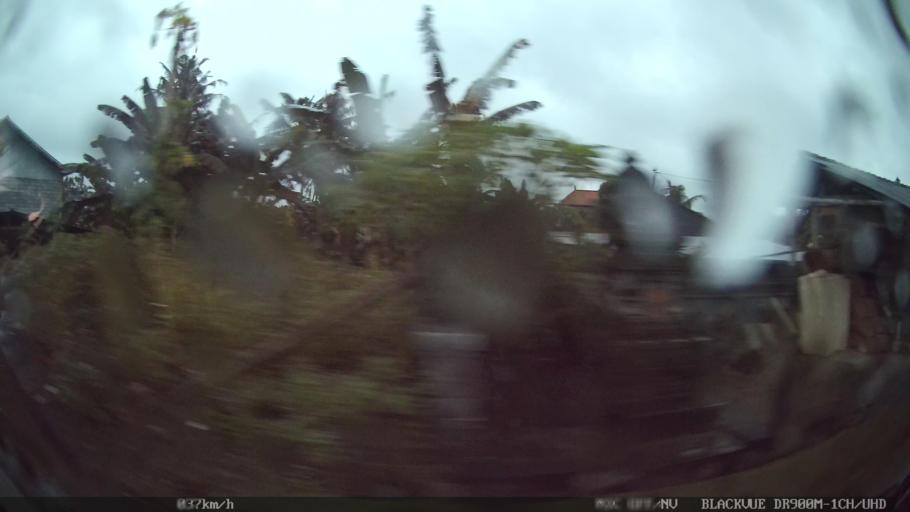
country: ID
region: Bali
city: Banjar Sedang
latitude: -8.5608
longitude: 115.2514
